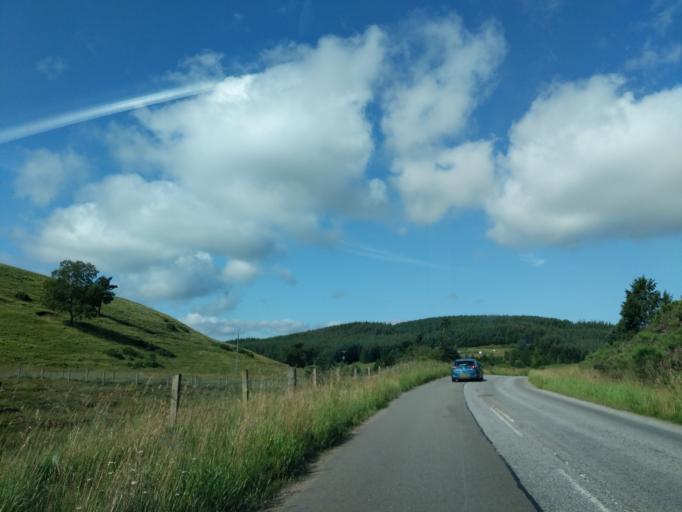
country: GB
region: Scotland
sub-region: Moray
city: Dufftown
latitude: 57.3724
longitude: -3.2447
